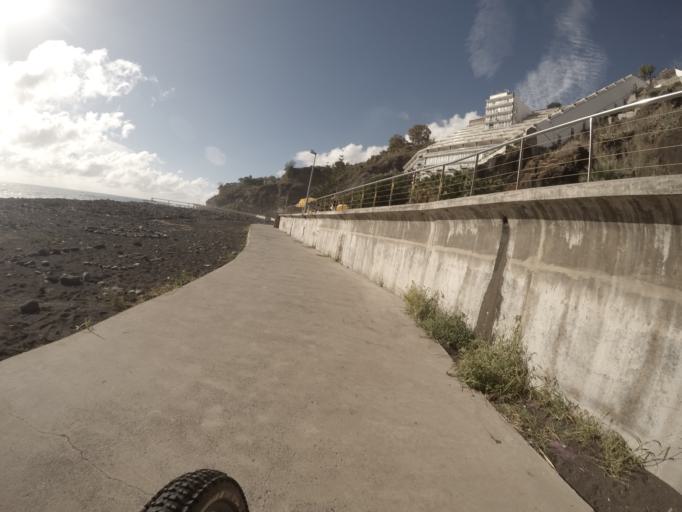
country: PT
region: Madeira
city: Camara de Lobos
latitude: 32.6427
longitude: -16.9585
